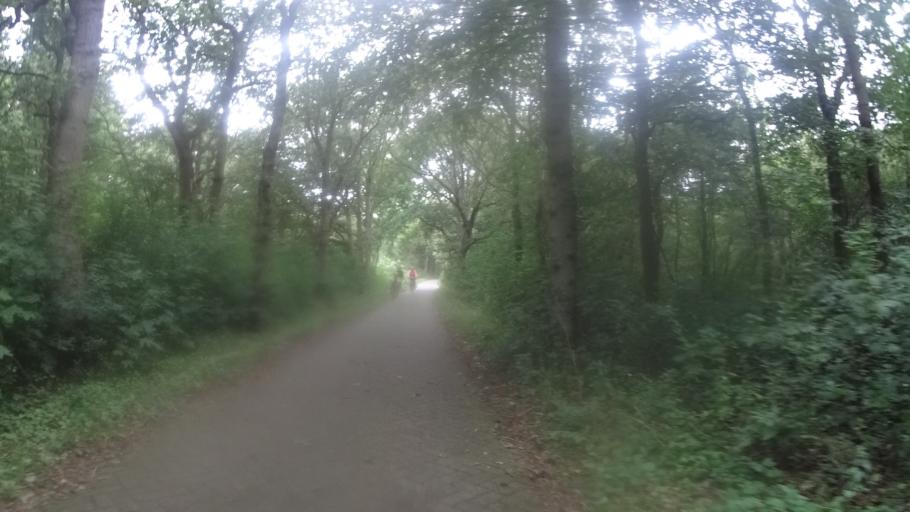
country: NL
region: North Holland
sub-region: Gemeente Castricum
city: Castricum
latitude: 52.5535
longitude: 4.6385
